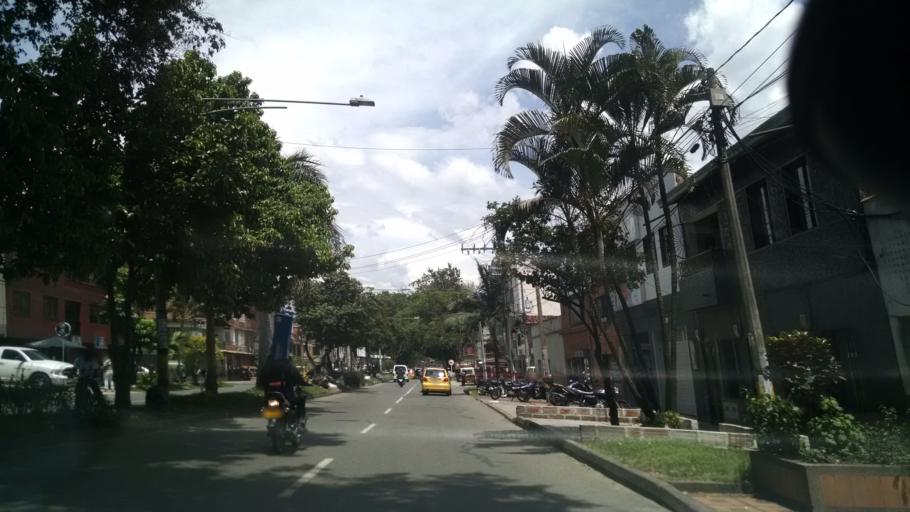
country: CO
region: Antioquia
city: Medellin
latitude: 6.2274
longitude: -75.5833
